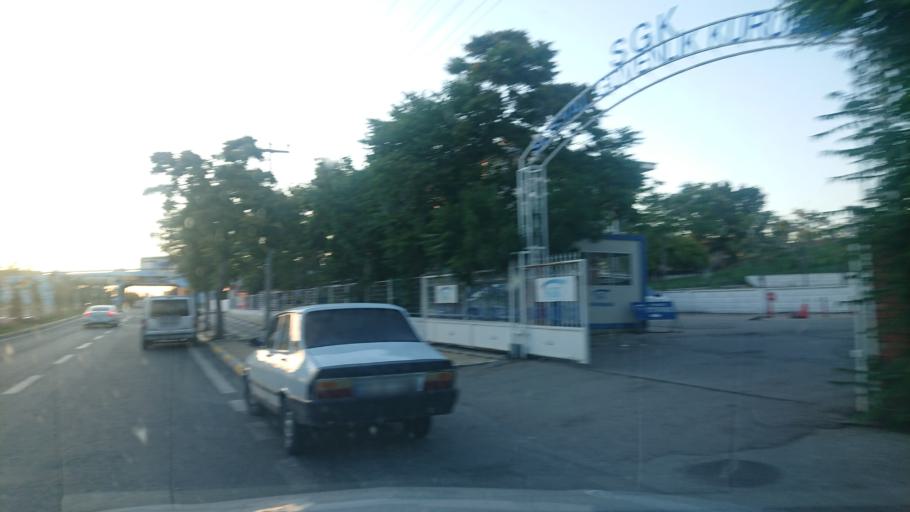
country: TR
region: Aksaray
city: Aksaray
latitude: 38.4000
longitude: 34.0194
